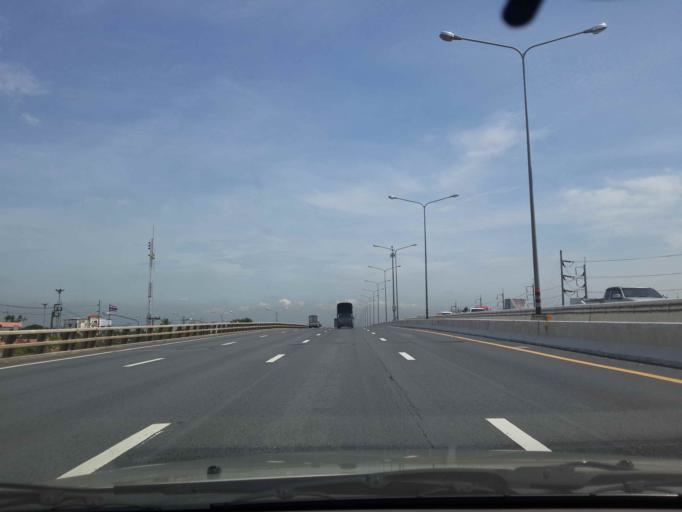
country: TH
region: Bangkok
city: Lat Krabang
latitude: 13.7101
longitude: 100.8201
